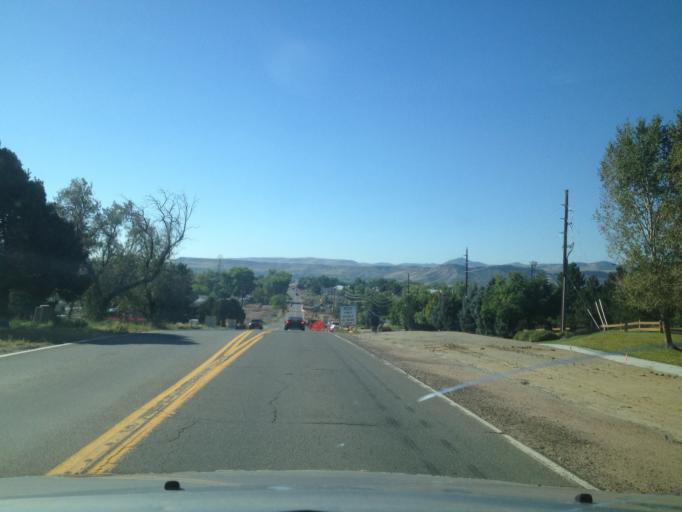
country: US
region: Colorado
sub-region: Jefferson County
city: Applewood
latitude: 39.8039
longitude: -105.1746
